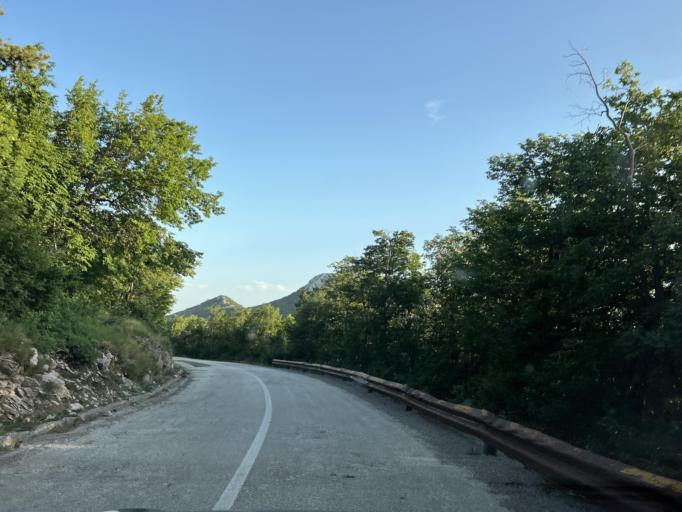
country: HR
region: Primorsko-Goranska
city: Skrljevo
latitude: 45.3880
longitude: 14.5599
